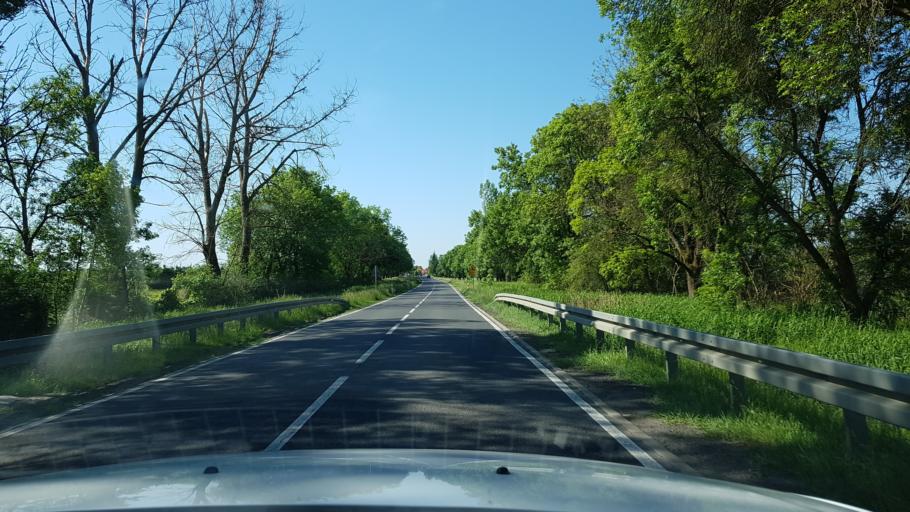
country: PL
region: West Pomeranian Voivodeship
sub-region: Powiat gryfinski
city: Mieszkowice
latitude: 52.7981
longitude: 14.4970
